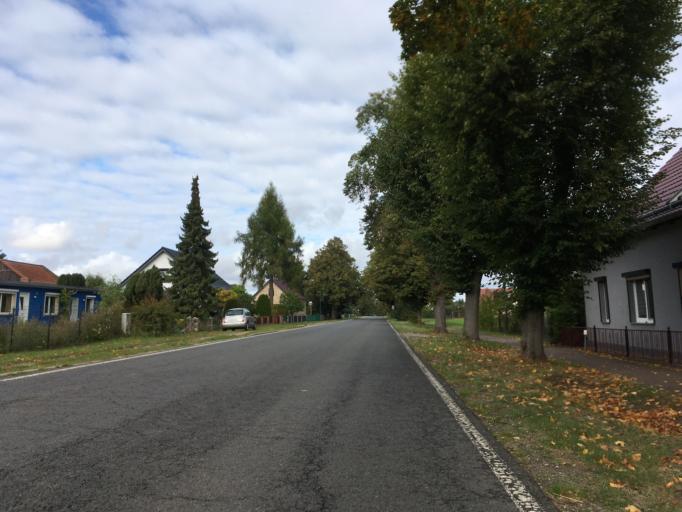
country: DE
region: Brandenburg
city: Oderberg
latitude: 52.9129
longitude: 14.1183
